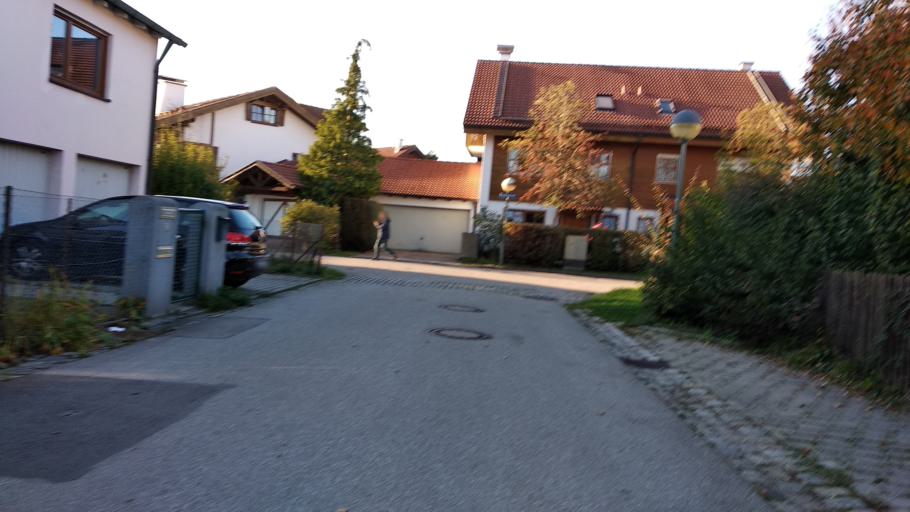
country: DE
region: Bavaria
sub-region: Upper Bavaria
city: Vaterstetten
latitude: 48.1069
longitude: 11.7653
